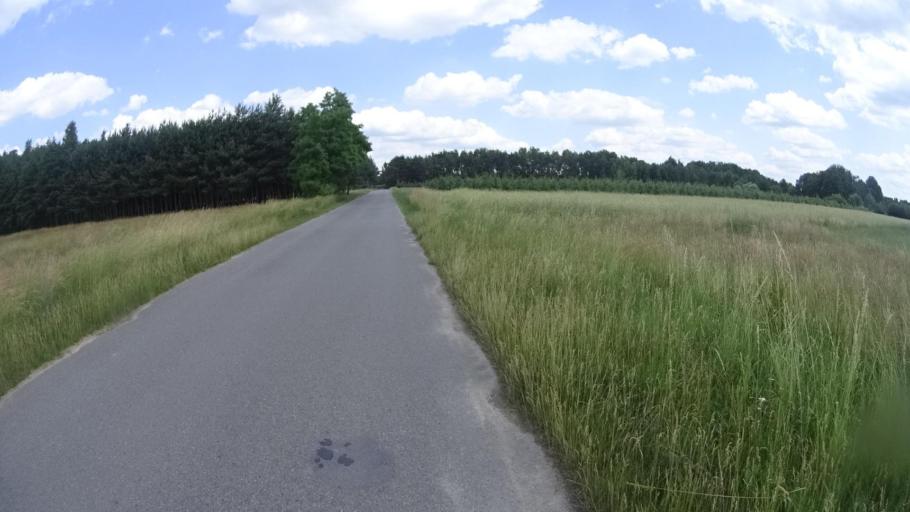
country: PL
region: Masovian Voivodeship
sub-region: Powiat grojecki
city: Goszczyn
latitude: 51.6961
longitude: 20.8778
